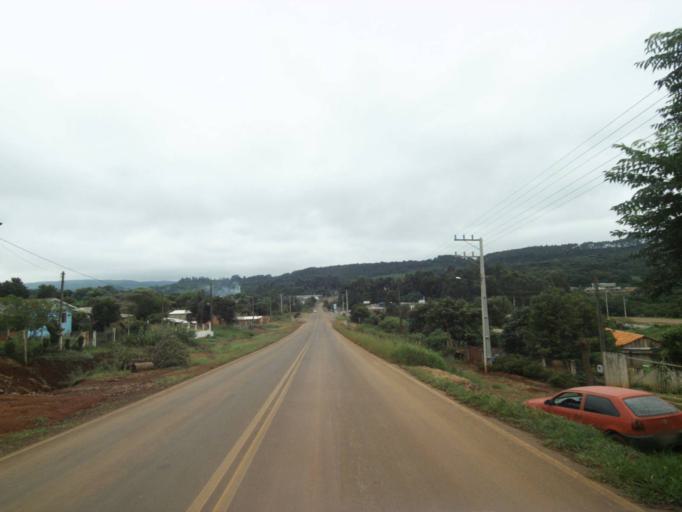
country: BR
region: Parana
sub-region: Pitanga
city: Pitanga
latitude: -24.9300
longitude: -51.8753
